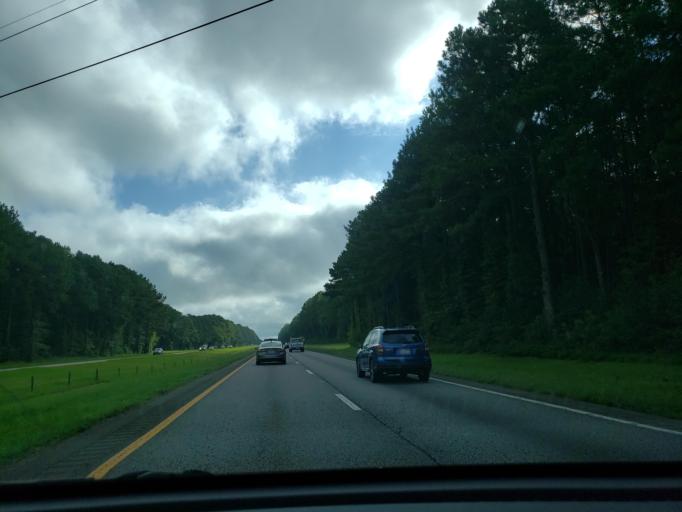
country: US
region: North Carolina
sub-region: Wake County
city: Zebulon
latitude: 35.8612
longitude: -78.2680
